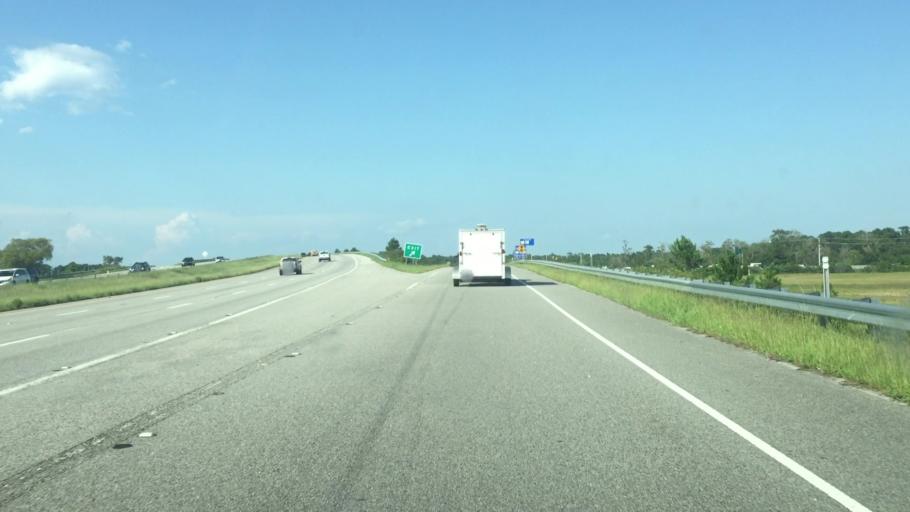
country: US
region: South Carolina
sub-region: Horry County
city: North Myrtle Beach
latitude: 33.8404
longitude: -78.7039
